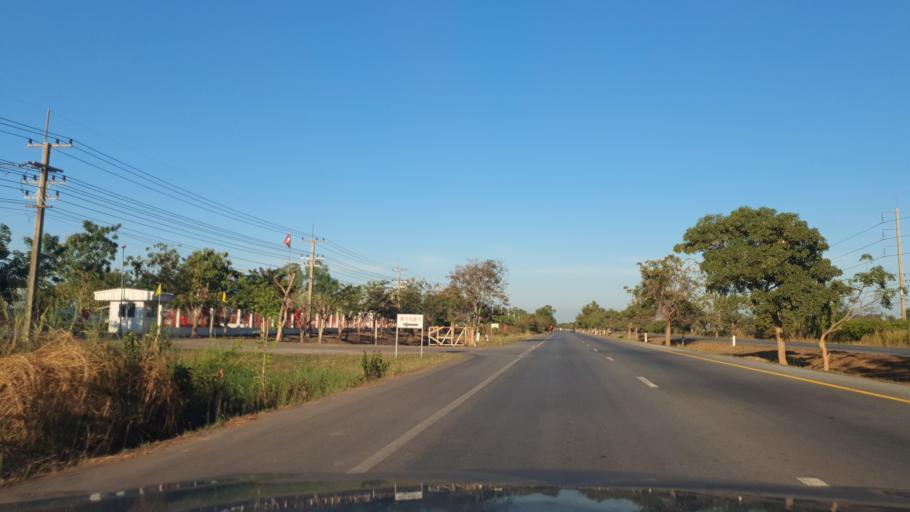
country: TH
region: Phitsanulok
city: Phitsanulok
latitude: 16.8612
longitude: 100.3023
